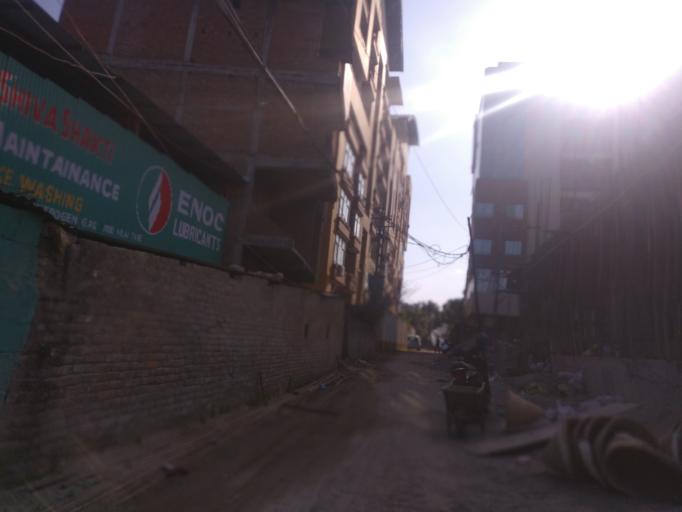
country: NP
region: Central Region
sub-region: Bagmati Zone
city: Patan
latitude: 27.6869
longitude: 85.3204
